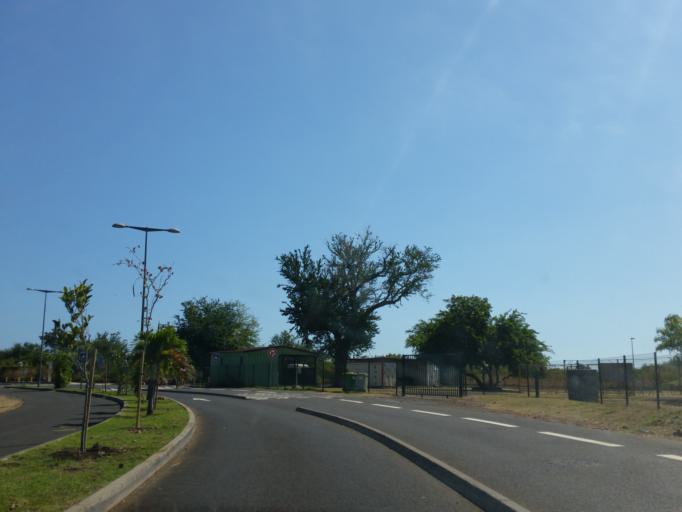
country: RE
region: Reunion
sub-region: Reunion
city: Saint-Paul
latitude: -20.9810
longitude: 55.2926
